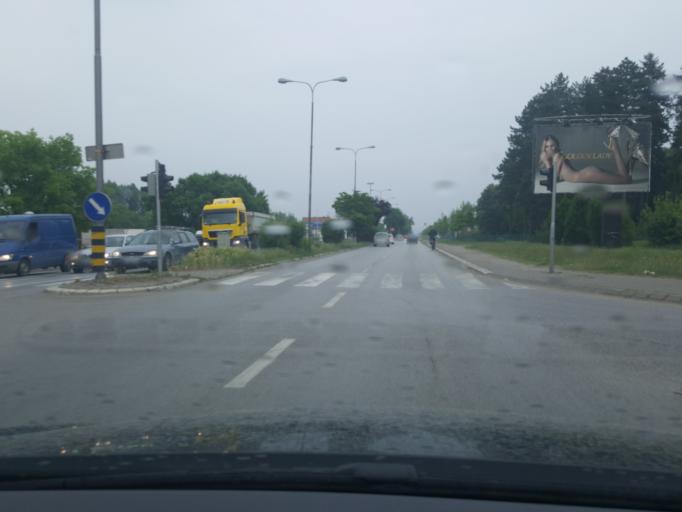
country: RS
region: Central Serbia
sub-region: Kolubarski Okrug
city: Valjevo
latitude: 44.2746
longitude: 19.9079
